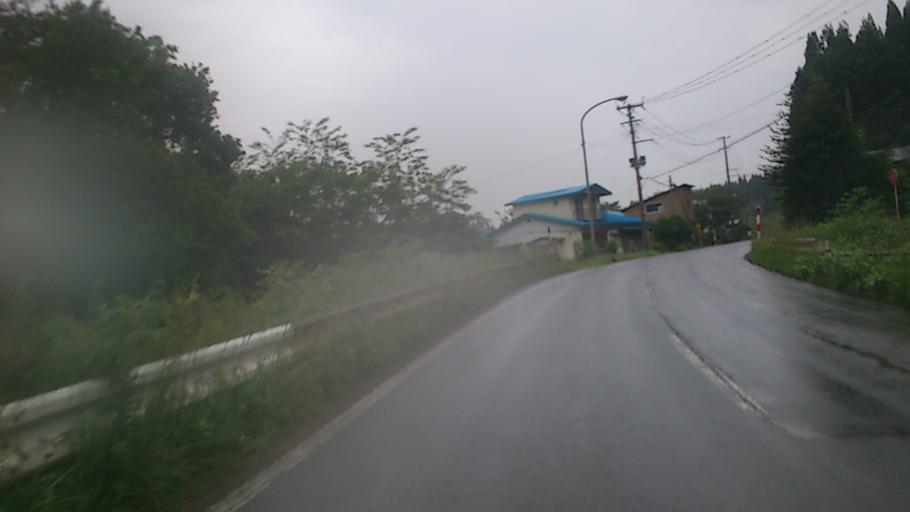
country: JP
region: Akita
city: Takanosu
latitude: 40.2446
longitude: 140.2476
